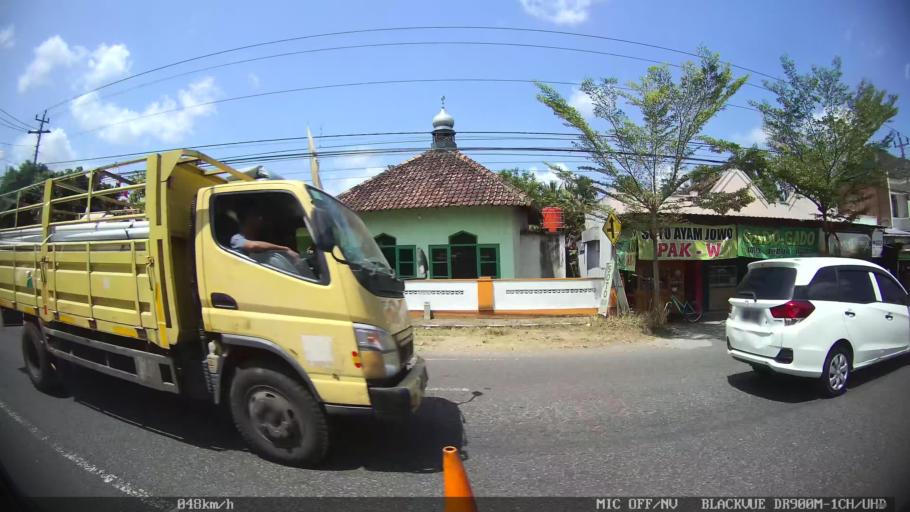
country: ID
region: Daerah Istimewa Yogyakarta
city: Pandak
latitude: -7.9098
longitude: 110.2968
